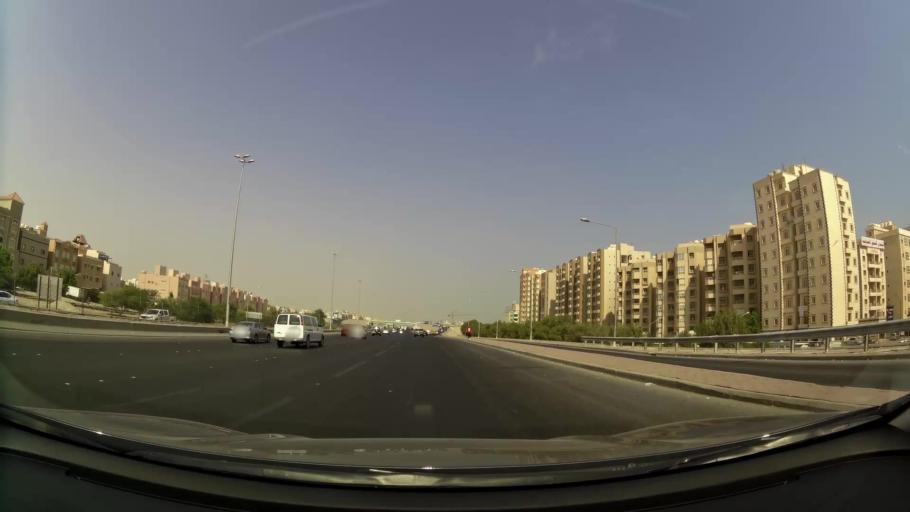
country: KW
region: Al Ahmadi
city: Al Fintas
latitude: 29.1796
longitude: 48.1137
